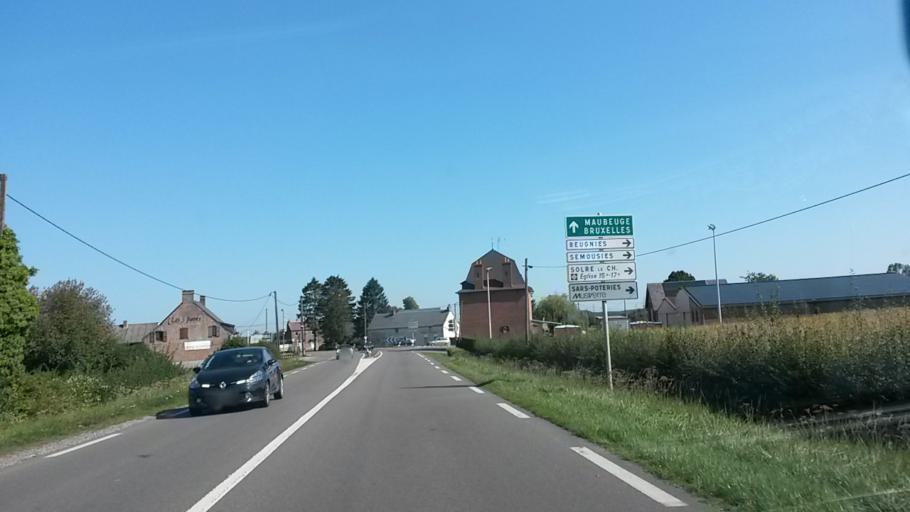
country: FR
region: Nord-Pas-de-Calais
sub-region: Departement du Nord
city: Avesnelles
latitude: 50.1536
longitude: 3.9541
